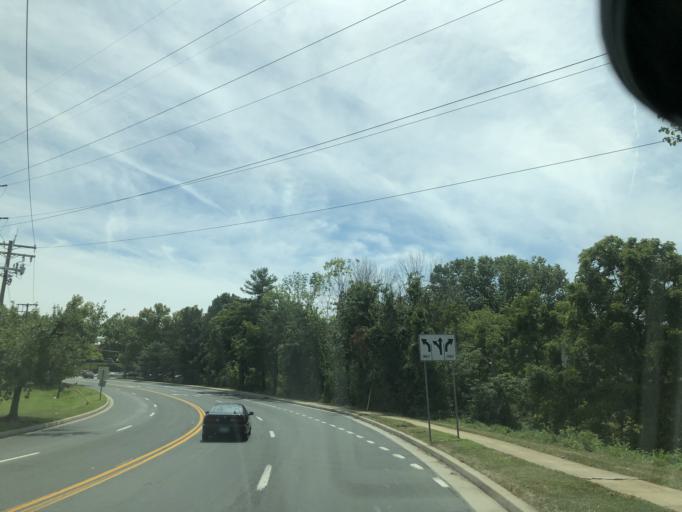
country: US
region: Maryland
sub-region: Howard County
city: Savage
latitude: 39.1805
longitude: -76.8284
